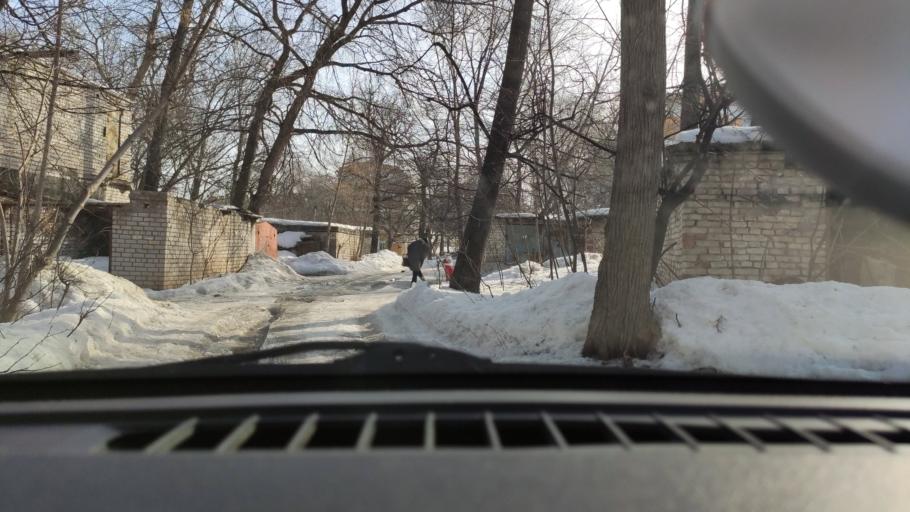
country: RU
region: Samara
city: Petra-Dubrava
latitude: 53.2790
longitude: 50.2684
